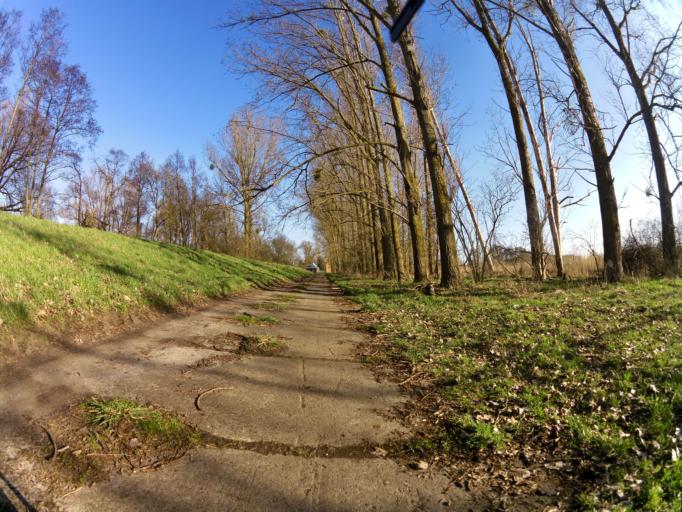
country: PL
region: West Pomeranian Voivodeship
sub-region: Powiat policki
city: Nowe Warpno
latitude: 53.6999
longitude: 14.3652
